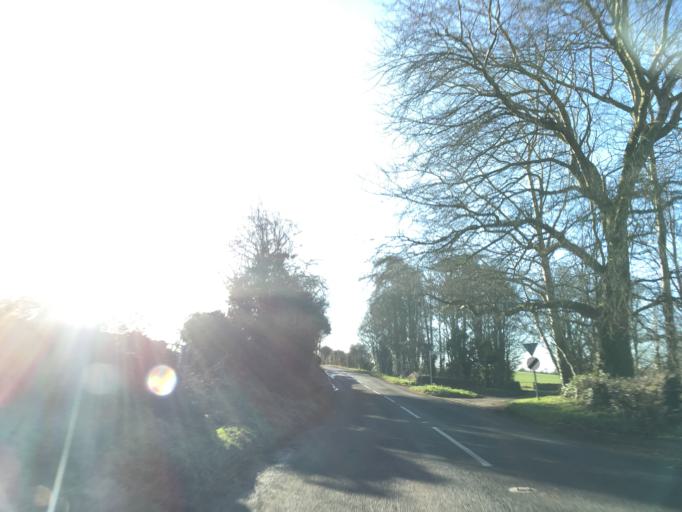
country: GB
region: England
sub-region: Wiltshire
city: Luckington
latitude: 51.5464
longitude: -2.2468
